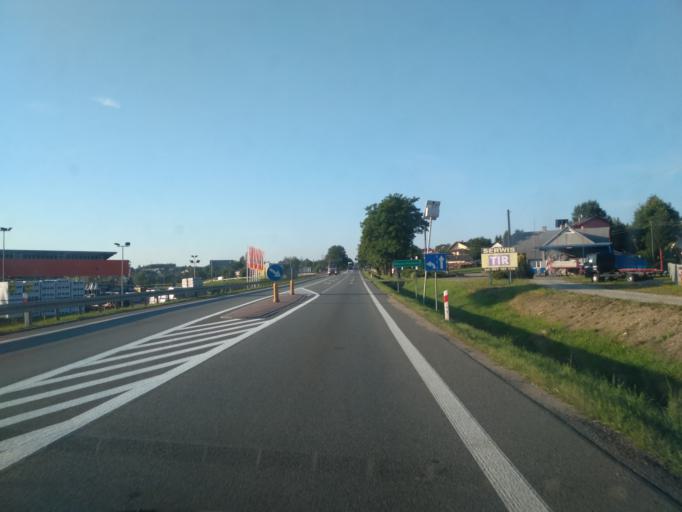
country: PL
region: Subcarpathian Voivodeship
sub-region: Powiat krosnienski
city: Miejsce Piastowe
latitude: 49.6458
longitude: 21.7837
